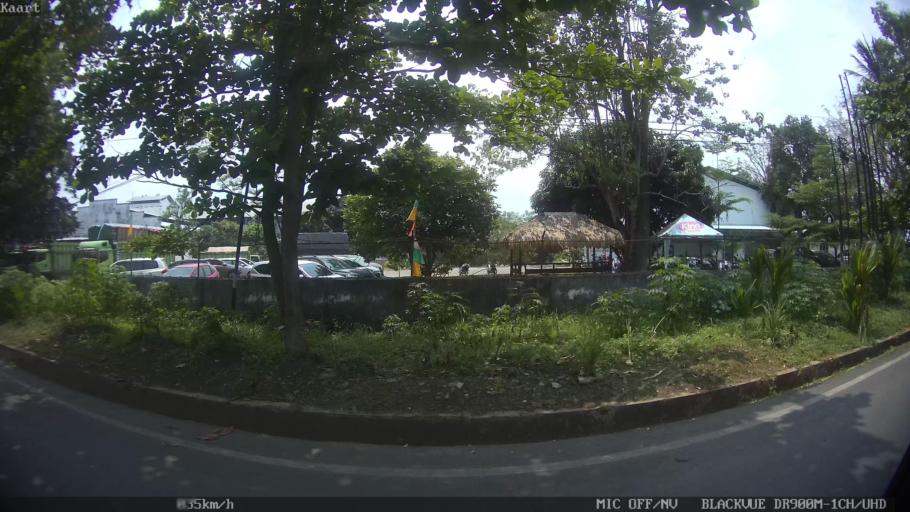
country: ID
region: Lampung
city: Bandarlampung
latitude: -5.4379
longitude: 105.2889
